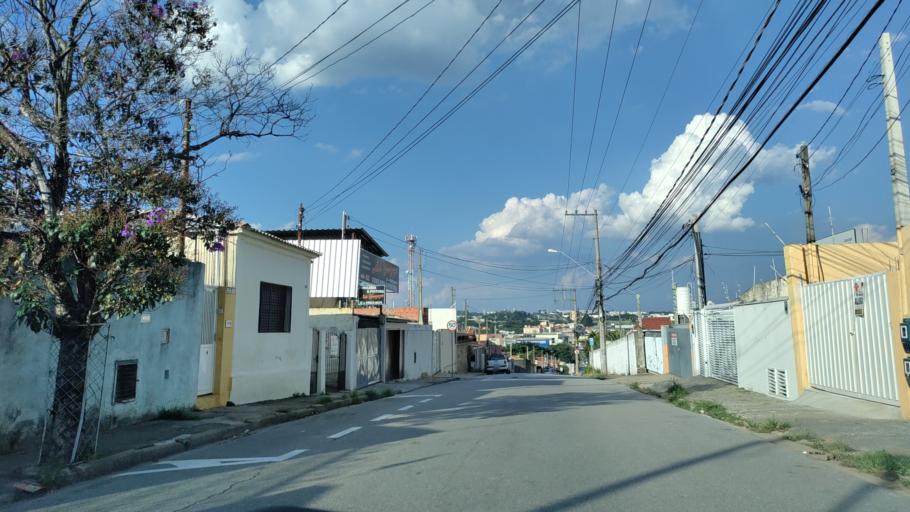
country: BR
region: Sao Paulo
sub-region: Sorocaba
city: Sorocaba
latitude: -23.4786
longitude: -47.4452
